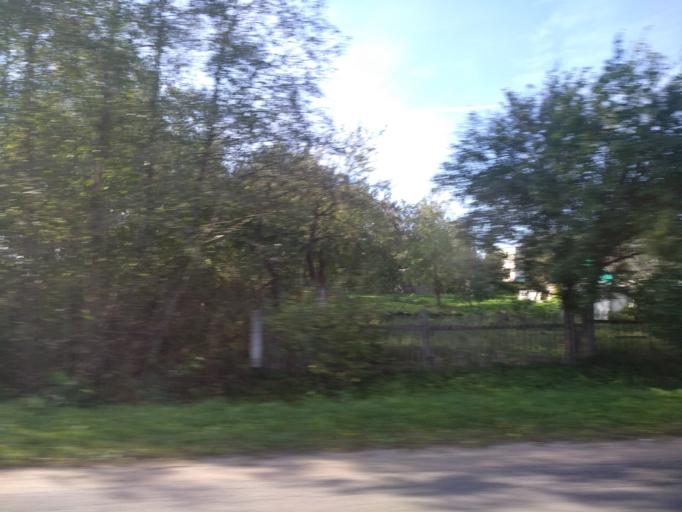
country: BY
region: Vitebsk
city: Mosar
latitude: 55.1393
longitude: 27.1945
